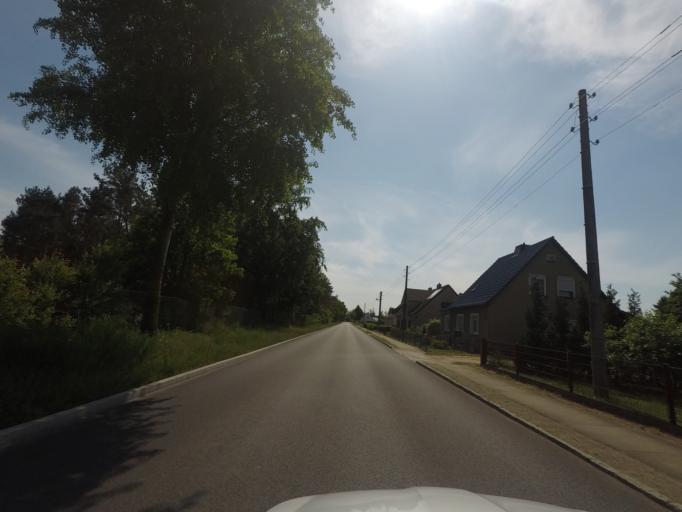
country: DE
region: Brandenburg
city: Britz
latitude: 52.8766
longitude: 13.8135
